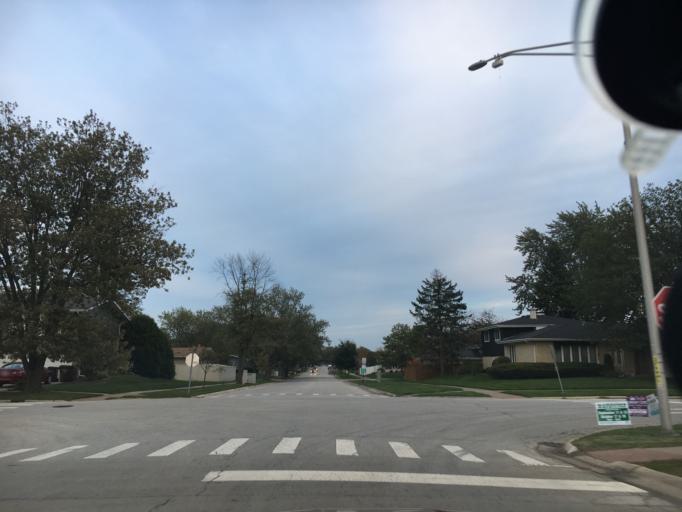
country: US
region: Illinois
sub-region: Cook County
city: Oak Forest
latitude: 41.6098
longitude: -87.7760
